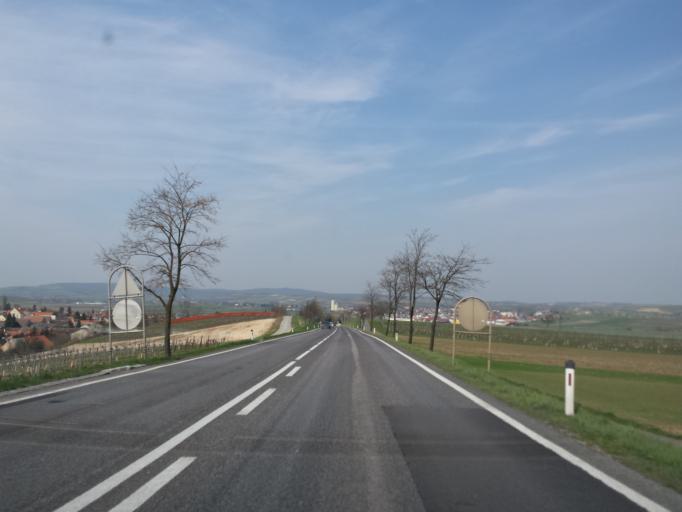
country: AT
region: Lower Austria
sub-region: Politischer Bezirk Mistelbach
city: Poysdorf
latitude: 48.6435
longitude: 16.6372
